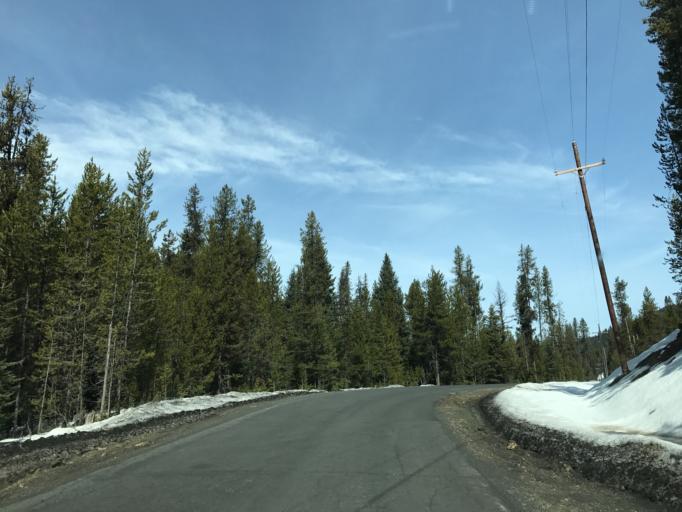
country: US
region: Idaho
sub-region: Valley County
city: McCall
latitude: 44.9622
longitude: -116.1699
